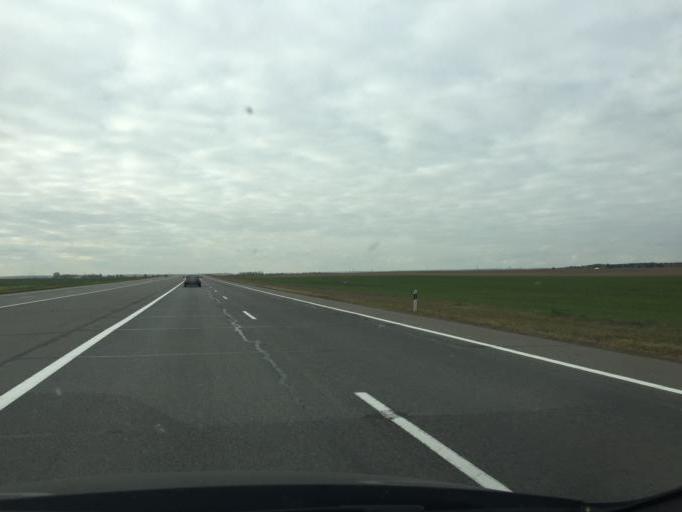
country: BY
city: Fanipol
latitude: 53.6835
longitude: 27.3036
